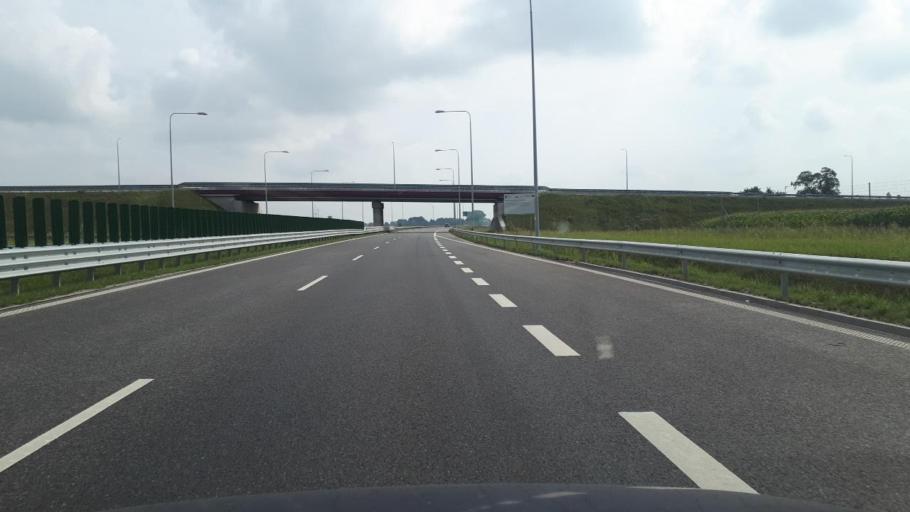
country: PL
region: Greater Poland Voivodeship
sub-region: Powiat kepinski
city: Kepno
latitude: 51.3090
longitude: 18.0152
